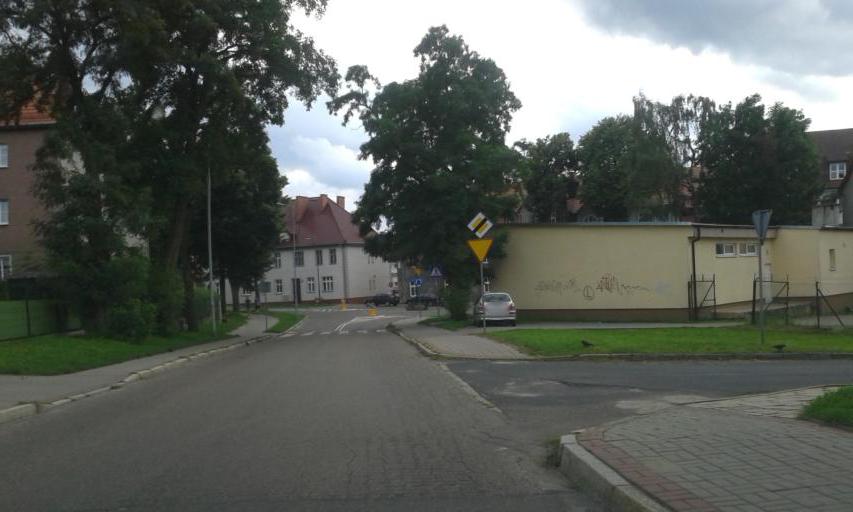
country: PL
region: West Pomeranian Voivodeship
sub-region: Powiat szczecinecki
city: Szczecinek
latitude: 53.7051
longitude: 16.7020
